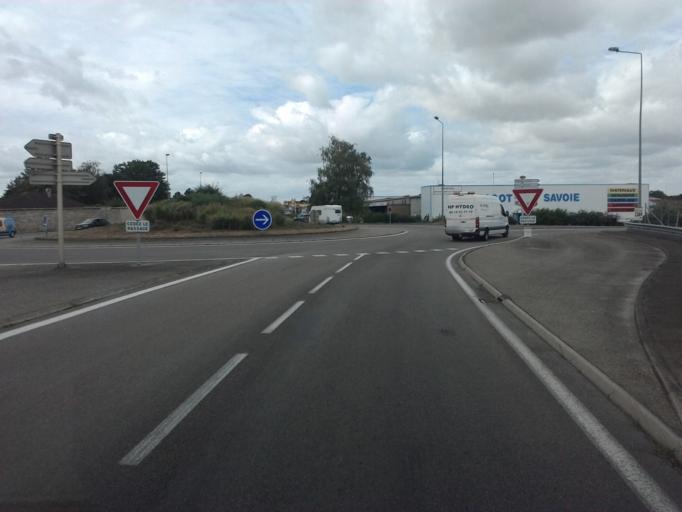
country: FR
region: Franche-Comte
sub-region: Departement du Jura
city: Tavaux
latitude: 47.0455
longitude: 5.4242
